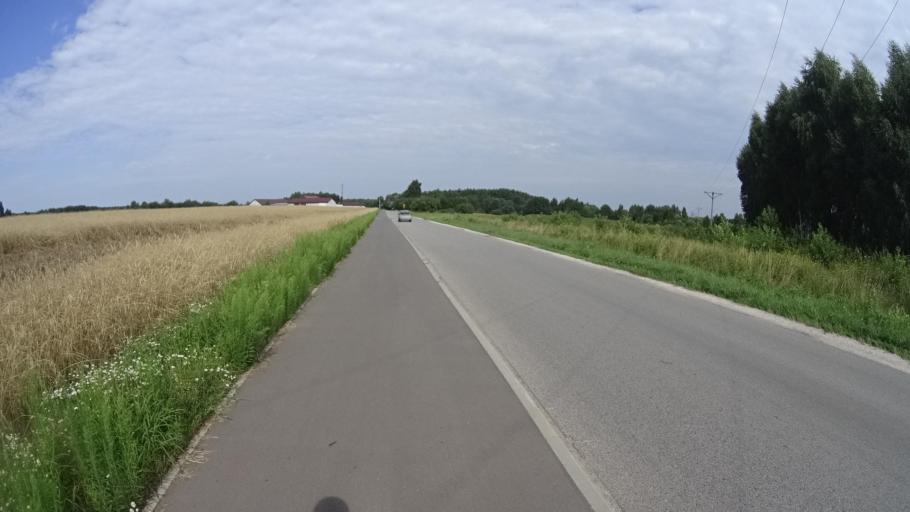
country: PL
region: Masovian Voivodeship
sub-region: Powiat piaseczynski
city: Tarczyn
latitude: 52.0139
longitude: 20.8007
